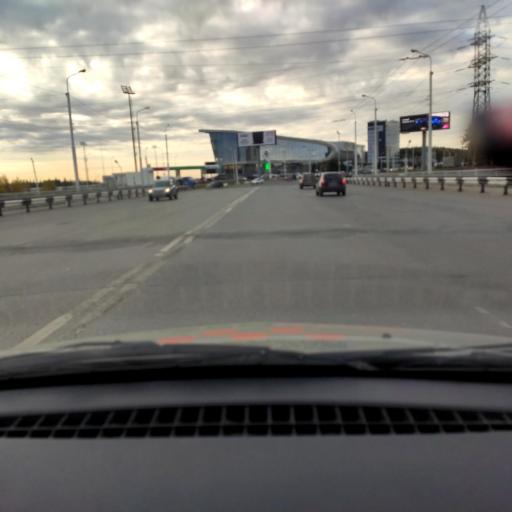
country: RU
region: Bashkortostan
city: Ufa
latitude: 54.7550
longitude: 56.0321
